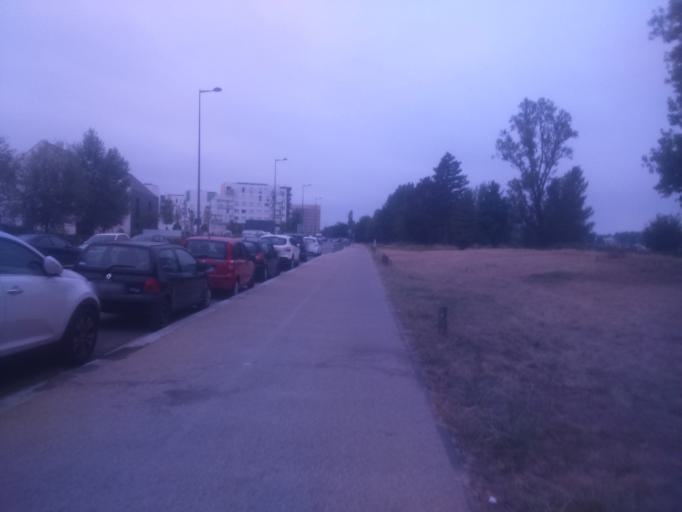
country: FR
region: Aquitaine
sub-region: Departement de la Gironde
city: Le Bouscat
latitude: 44.8825
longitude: -0.5723
